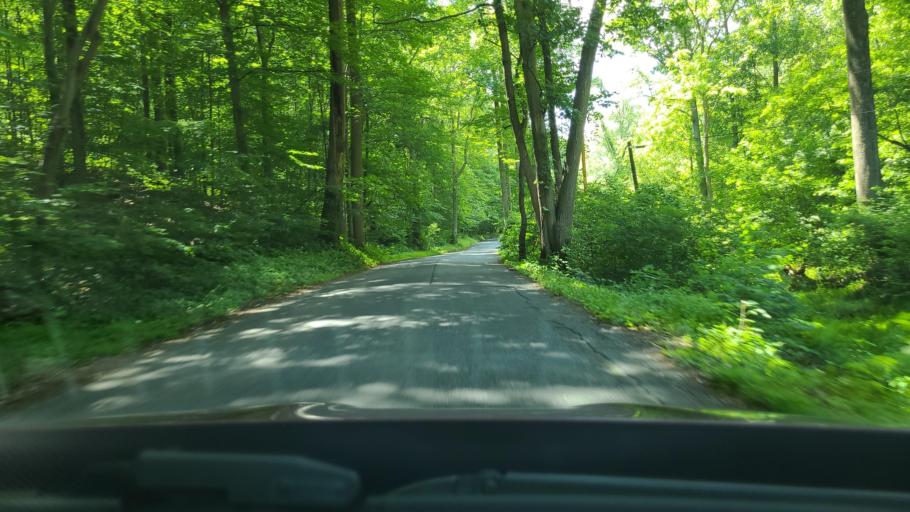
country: US
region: Maryland
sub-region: Montgomery County
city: Damascus
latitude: 39.2684
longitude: -77.2418
